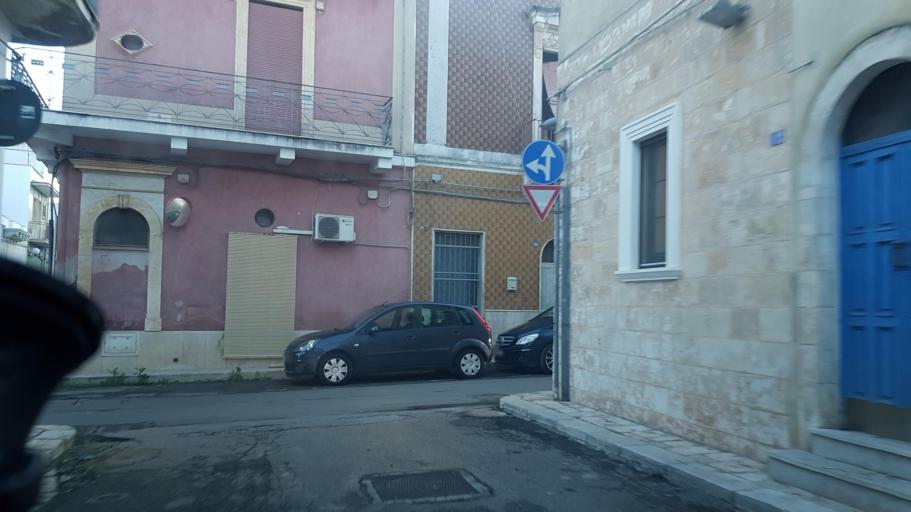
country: IT
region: Apulia
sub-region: Provincia di Brindisi
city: San Michele Salentino
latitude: 40.6305
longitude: 17.6342
